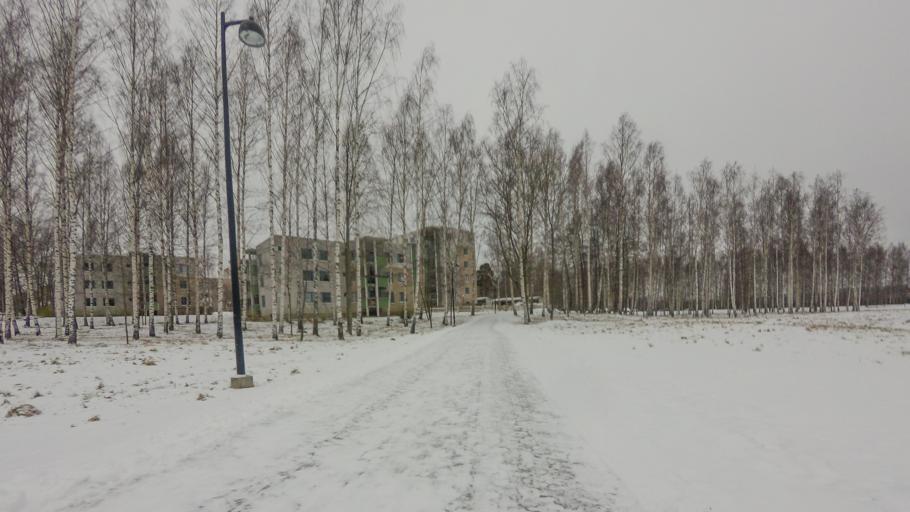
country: FI
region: Uusimaa
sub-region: Helsinki
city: Vantaa
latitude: 60.2006
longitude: 25.0693
